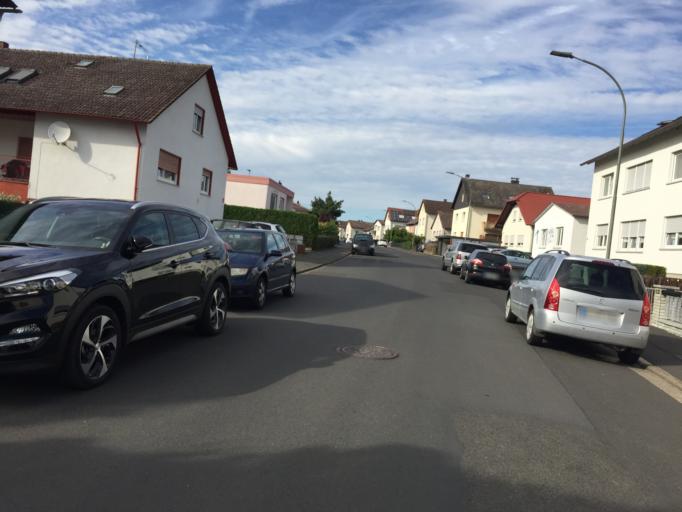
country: DE
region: Hesse
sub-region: Regierungsbezirk Darmstadt
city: Rockenberg
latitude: 50.4875
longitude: 8.7258
